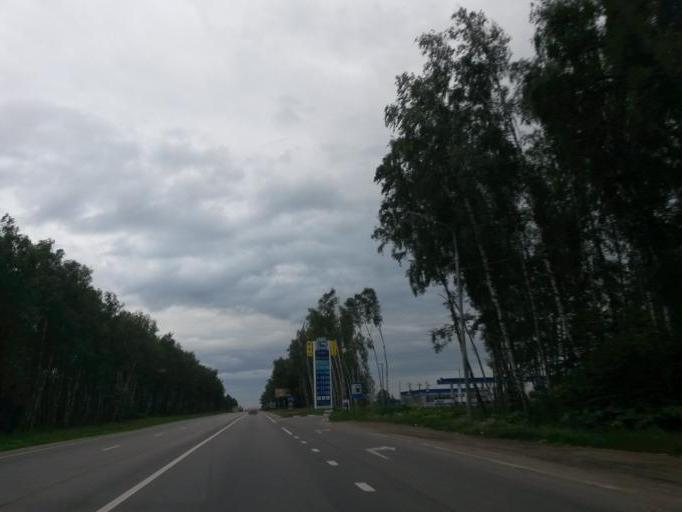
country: RU
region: Moskovskaya
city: Belyye Stolby
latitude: 55.2829
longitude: 37.8228
